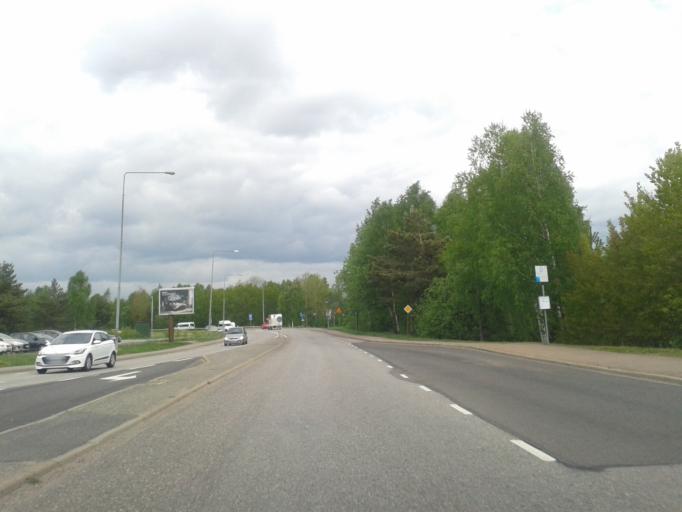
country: SE
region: Vaestra Goetaland
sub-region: Goteborg
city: Hammarkullen
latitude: 57.7855
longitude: 12.0477
